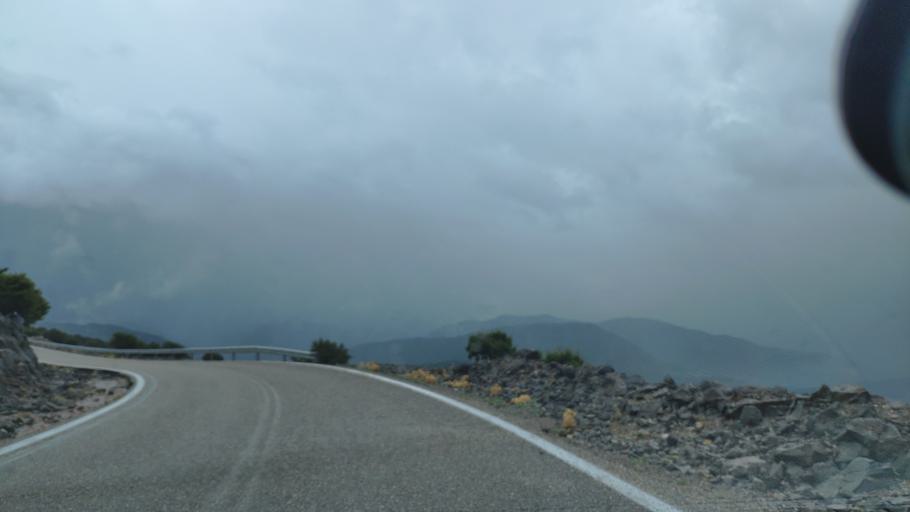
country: GR
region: West Greece
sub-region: Nomos Aitolias kai Akarnanias
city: Krikellos
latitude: 39.0753
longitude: 21.3972
